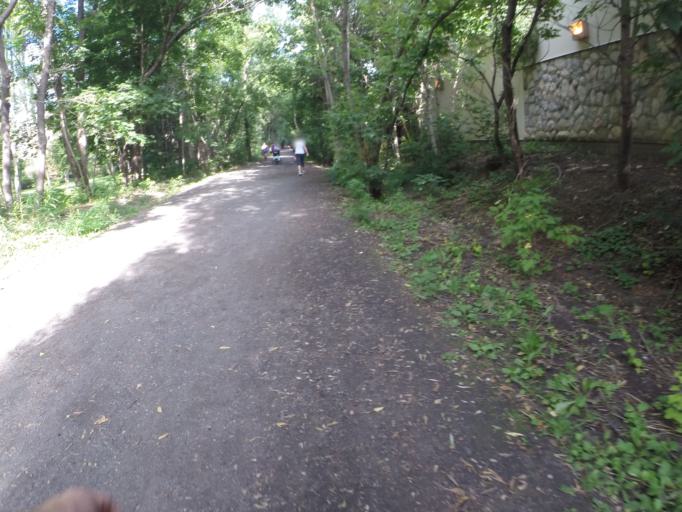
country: CA
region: Ontario
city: Toronto
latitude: 43.6982
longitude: -79.4061
